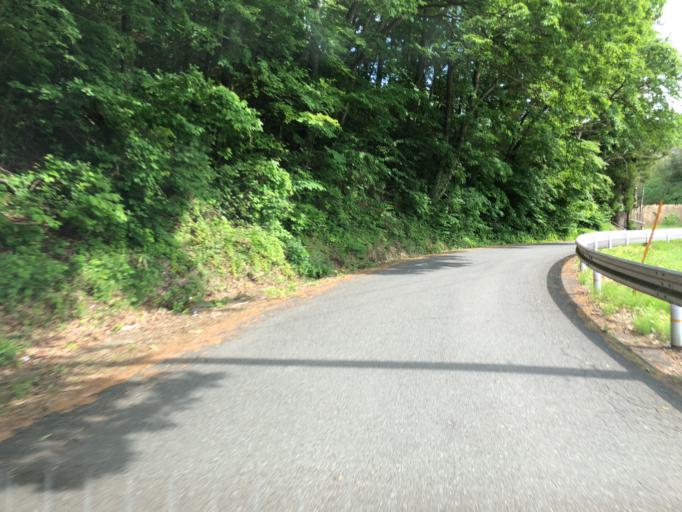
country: JP
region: Fukushima
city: Nihommatsu
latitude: 37.6268
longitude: 140.5125
